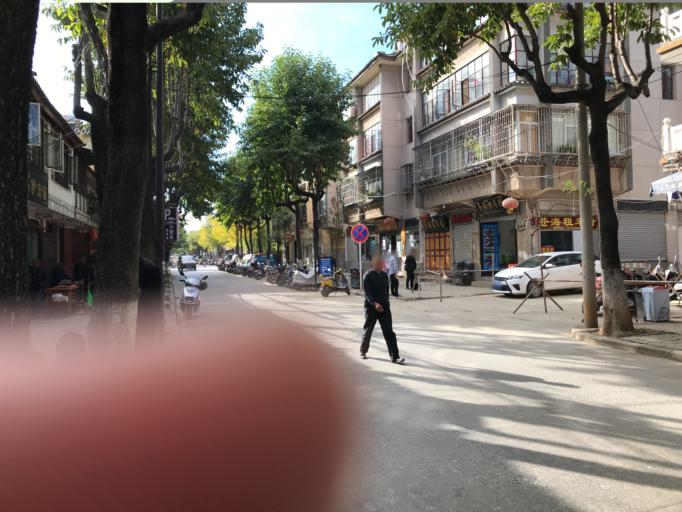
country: CN
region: Yunnan
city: Dali
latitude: 25.7011
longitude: 100.1639
